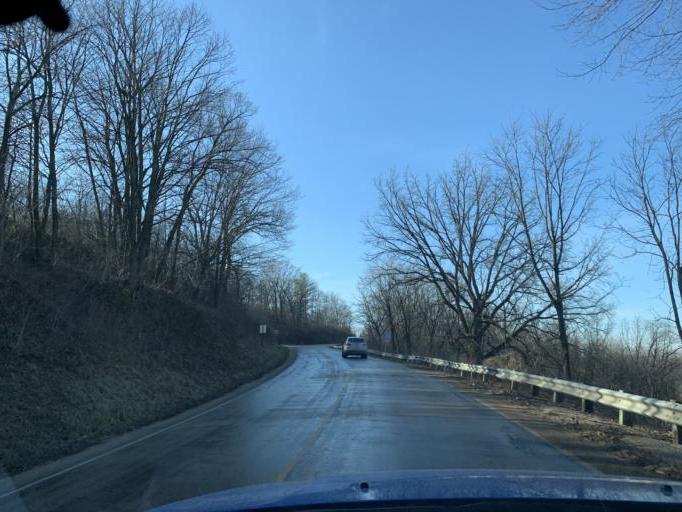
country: US
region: Wisconsin
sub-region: Iowa County
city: Barneveld
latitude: 42.8082
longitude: -89.8666
